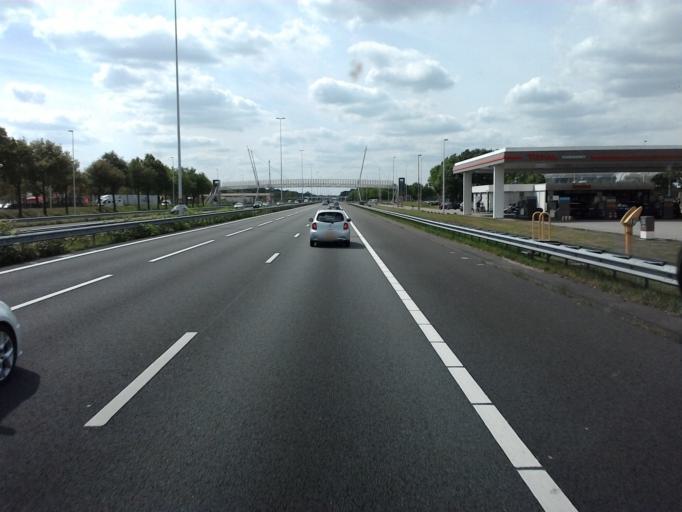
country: NL
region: Utrecht
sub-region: Gemeente Utrechtse Heuvelrug
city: Overberg
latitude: 52.0506
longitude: 5.4665
